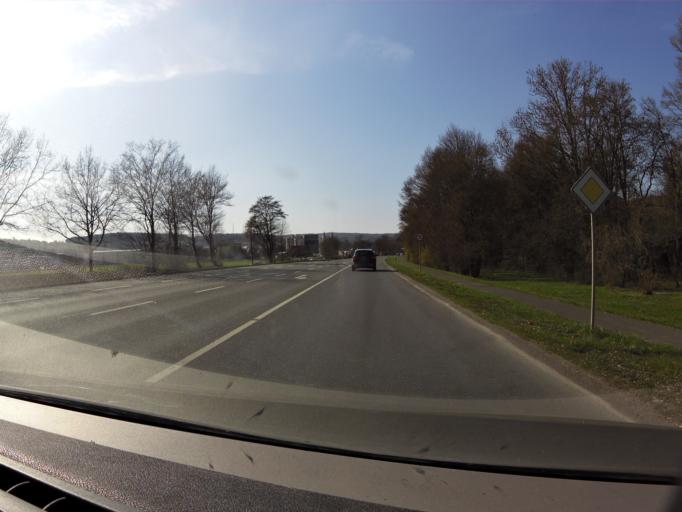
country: DE
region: Baden-Wuerttemberg
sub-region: Regierungsbezirk Stuttgart
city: Bad Mergentheim
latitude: 49.4903
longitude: 9.7908
